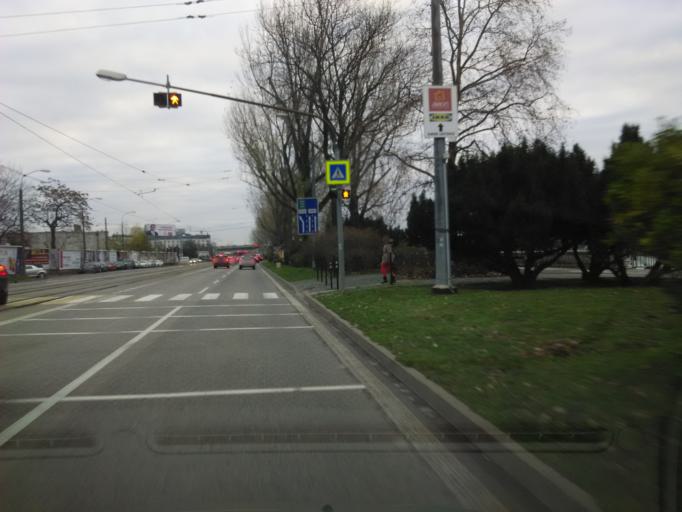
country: SK
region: Bratislavsky
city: Bratislava
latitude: 48.1399
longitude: 17.0983
